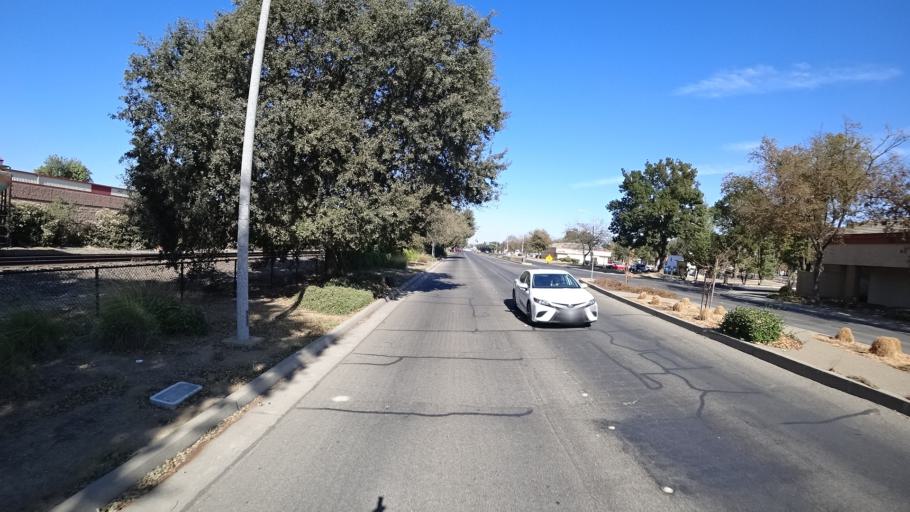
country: US
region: California
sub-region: Yolo County
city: Woodland
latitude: 38.6611
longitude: -121.7658
